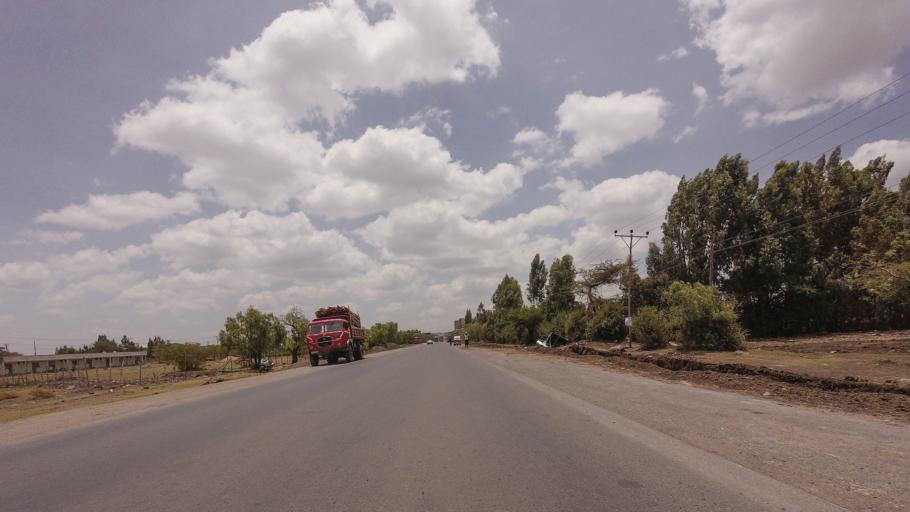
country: ET
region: Oromiya
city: Bishoftu
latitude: 8.7689
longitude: 38.9336
